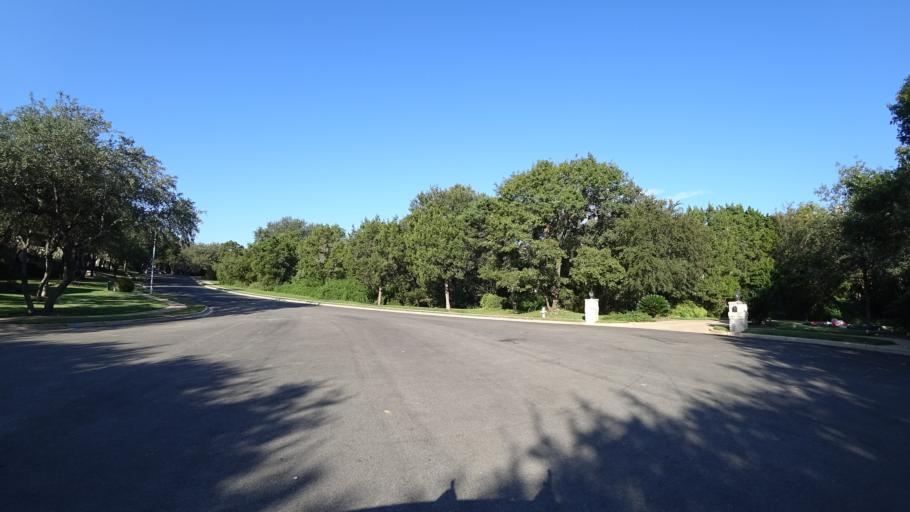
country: US
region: Texas
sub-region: Travis County
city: Rollingwood
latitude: 30.2687
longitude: -97.7940
